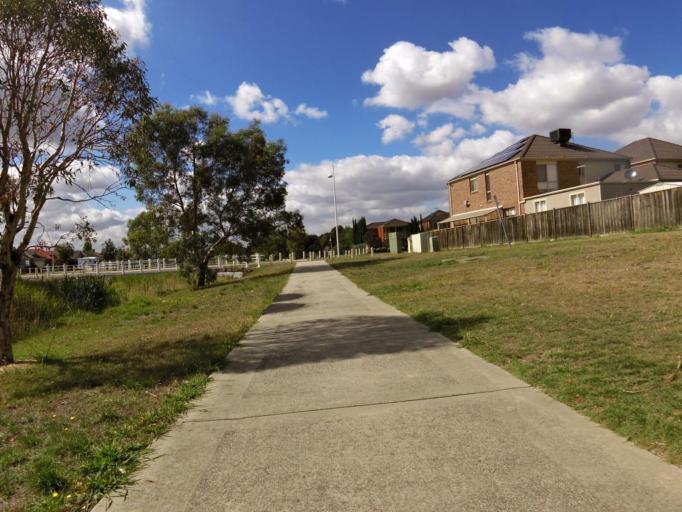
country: AU
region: Victoria
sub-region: Whittlesea
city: Mill Park
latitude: -37.6298
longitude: 145.0682
